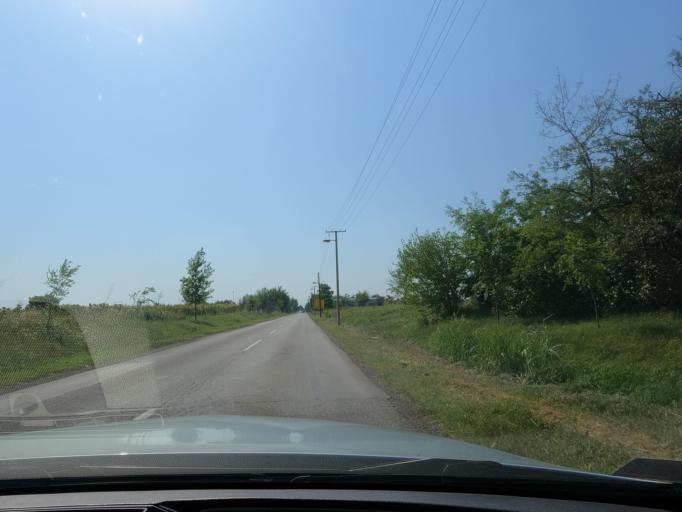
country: RS
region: Autonomna Pokrajina Vojvodina
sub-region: Severnobacki Okrug
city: Backa Topola
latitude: 45.8219
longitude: 19.6678
